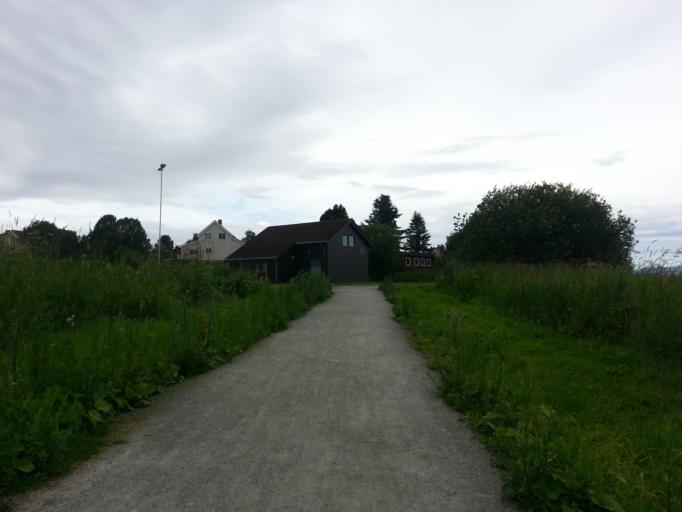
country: NO
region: Sor-Trondelag
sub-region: Trondheim
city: Trondheim
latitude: 63.4306
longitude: 10.5213
